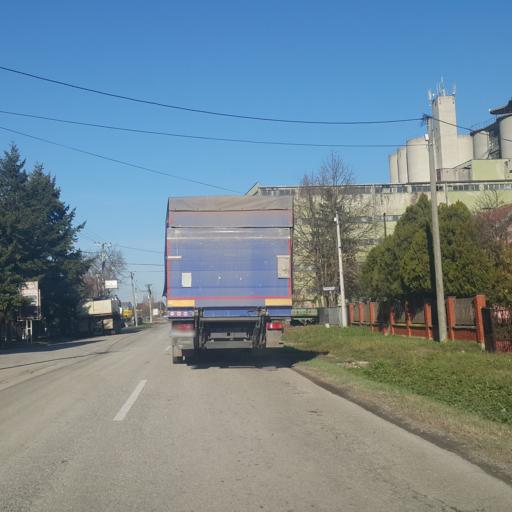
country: RS
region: Central Serbia
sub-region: Sumadijski Okrug
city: Lapovo
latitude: 44.2347
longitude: 21.0949
